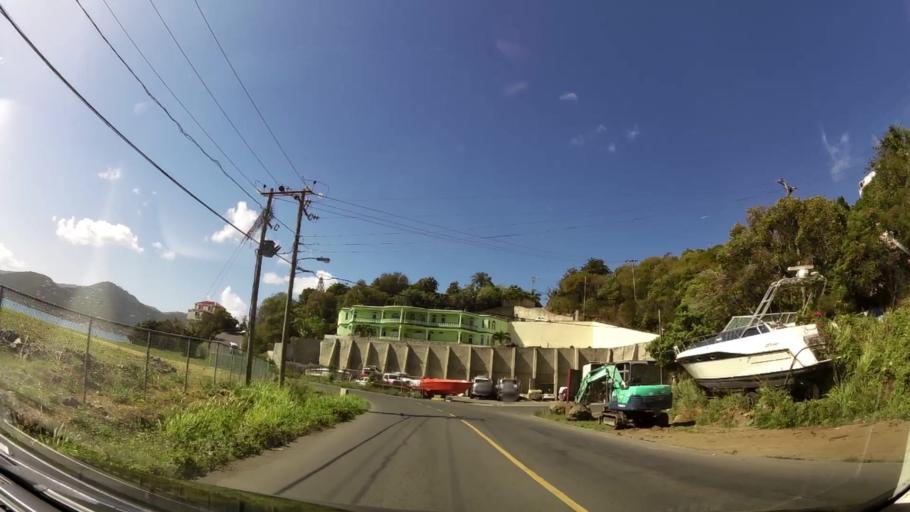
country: VG
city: Tortola
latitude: 18.4166
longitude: -64.5966
